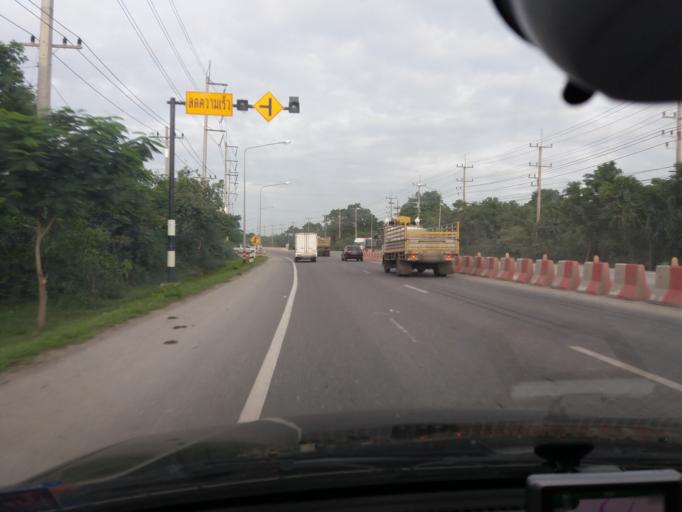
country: TH
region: Suphan Buri
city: U Thong
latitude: 14.3411
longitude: 99.8468
